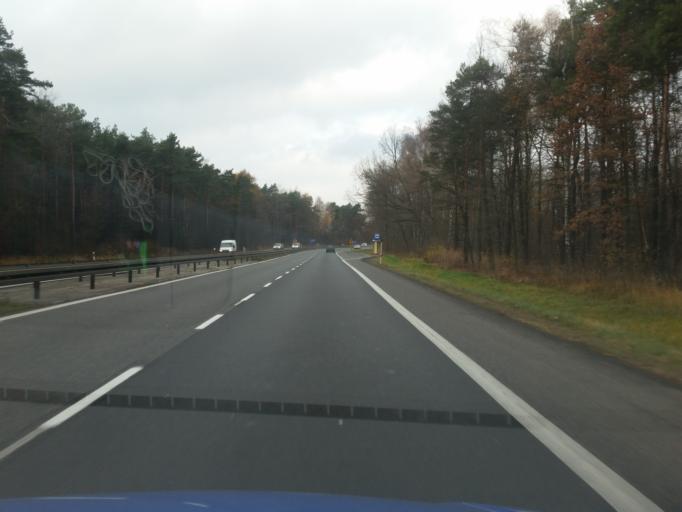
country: PL
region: Silesian Voivodeship
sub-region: Powiat myszkowski
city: Kozieglowy
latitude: 50.5383
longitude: 19.1851
